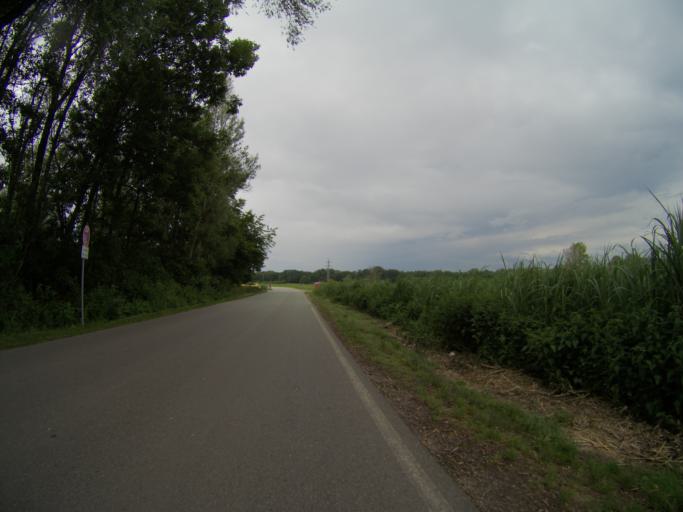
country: DE
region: Bavaria
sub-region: Upper Bavaria
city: Marzling
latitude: 48.3938
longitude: 11.7976
